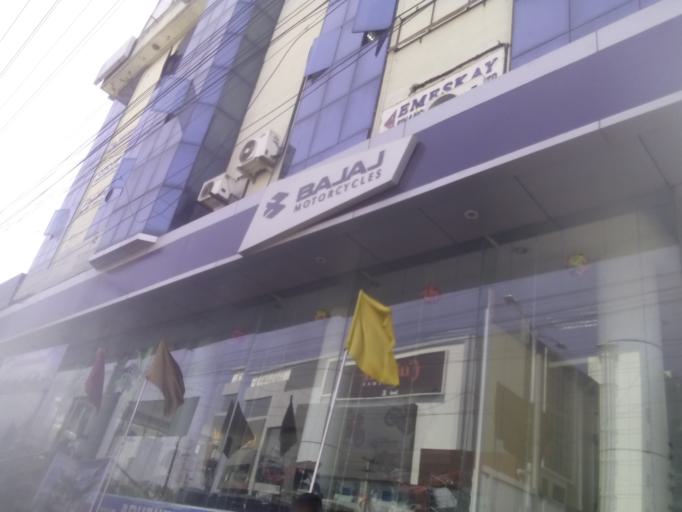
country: IN
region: Andhra Pradesh
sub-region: Krishna
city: Yanamalakuduru
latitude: 16.5000
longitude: 80.6537
